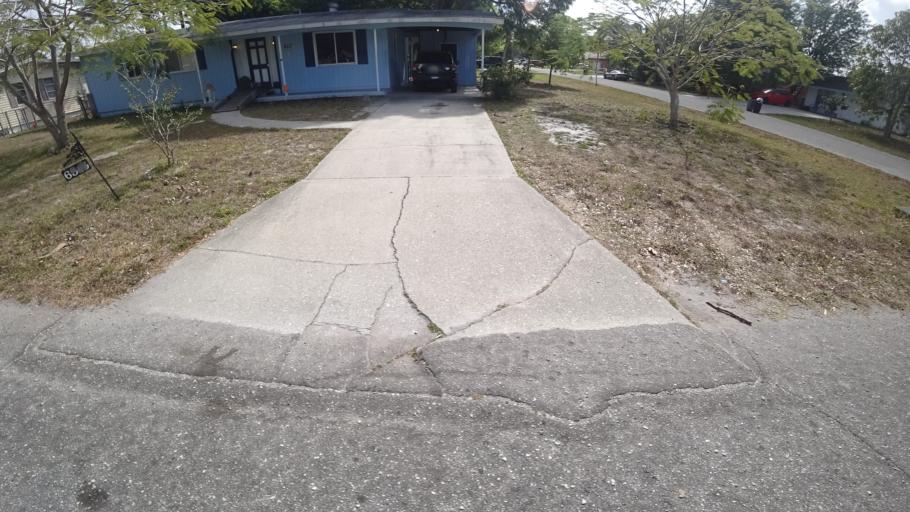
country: US
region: Florida
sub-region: Manatee County
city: Whitfield
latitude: 27.4247
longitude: -82.5658
